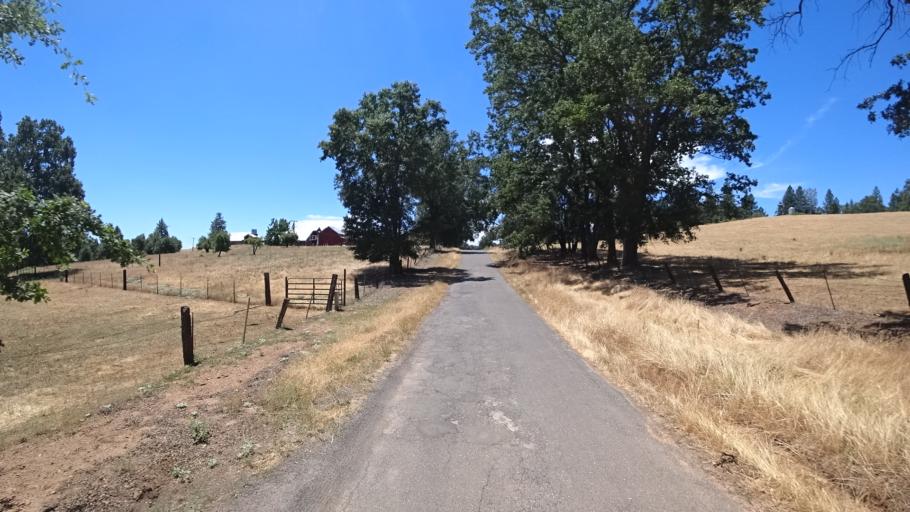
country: US
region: California
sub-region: Calaveras County
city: Forest Meadows
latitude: 38.2356
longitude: -120.4480
